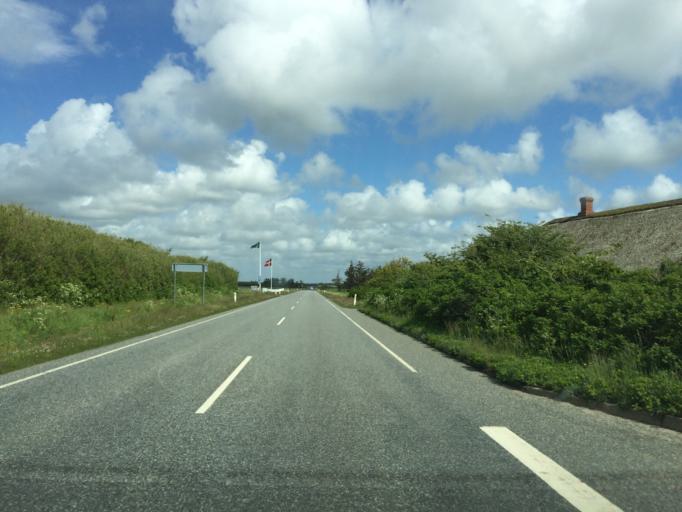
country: DK
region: Central Jutland
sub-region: Holstebro Kommune
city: Ulfborg
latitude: 56.3186
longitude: 8.1468
